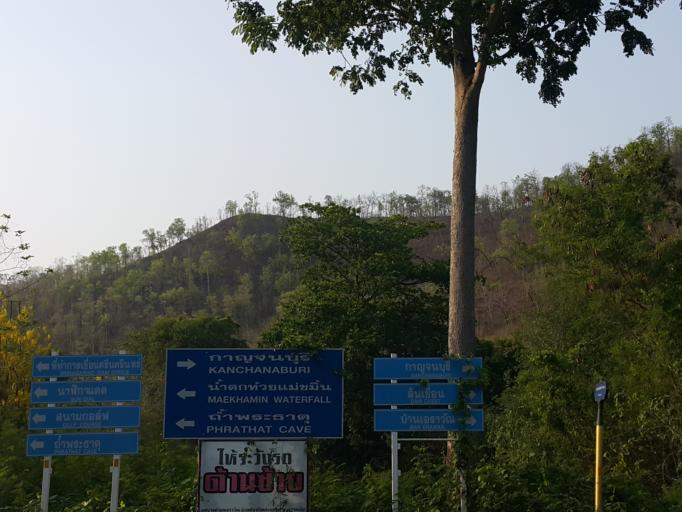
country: TH
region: Kanchanaburi
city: Si Sawat
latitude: 14.3845
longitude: 99.1360
